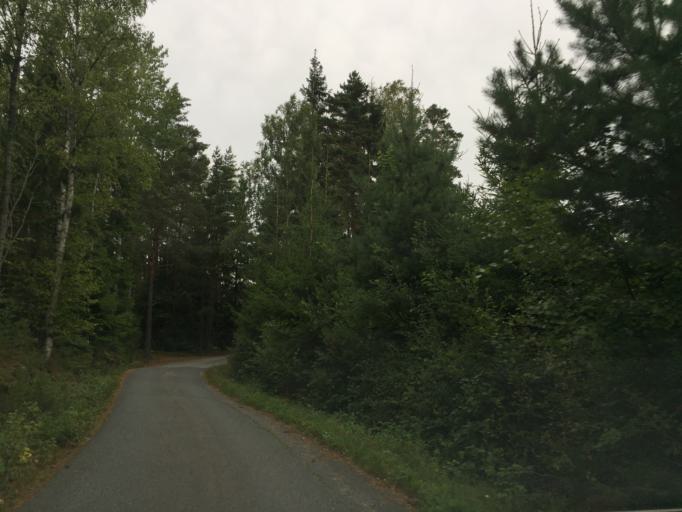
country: NO
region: Ostfold
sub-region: Hvaler
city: Skjaerhalden
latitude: 59.0786
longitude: 11.0054
